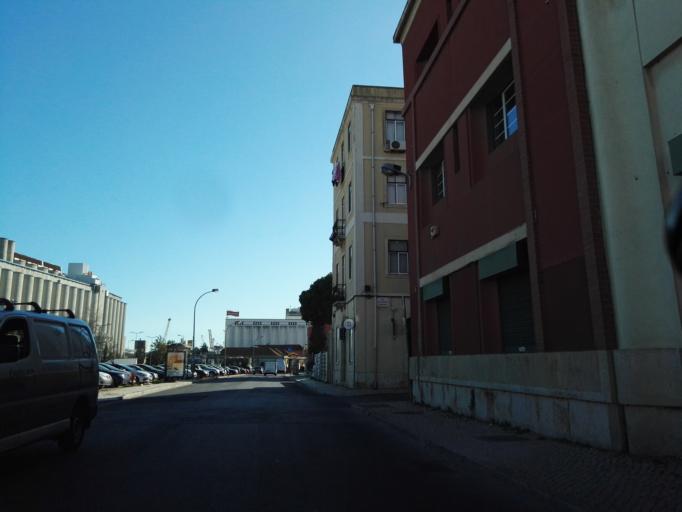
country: PT
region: Lisbon
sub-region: Lisbon
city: Lisbon
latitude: 38.7377
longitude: -9.1035
